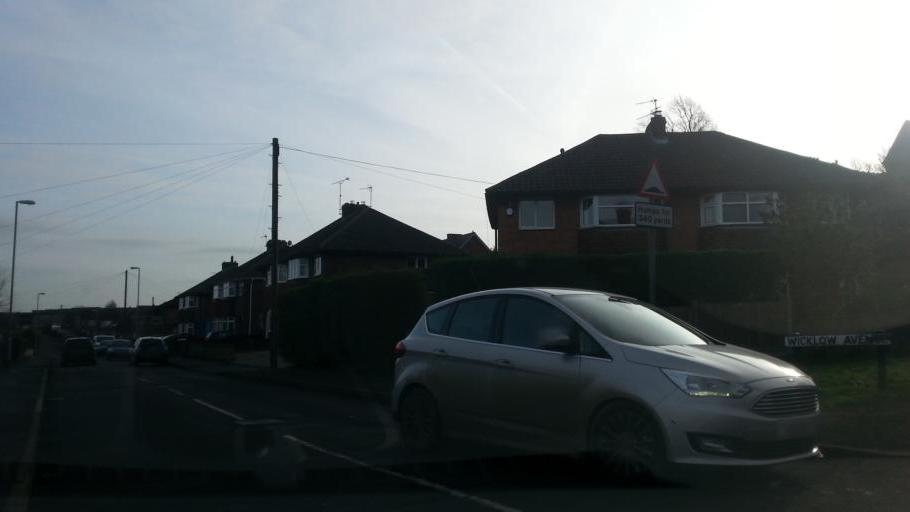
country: GB
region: England
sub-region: Leicestershire
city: Melton Mowbray
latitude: 52.7571
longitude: -0.8808
